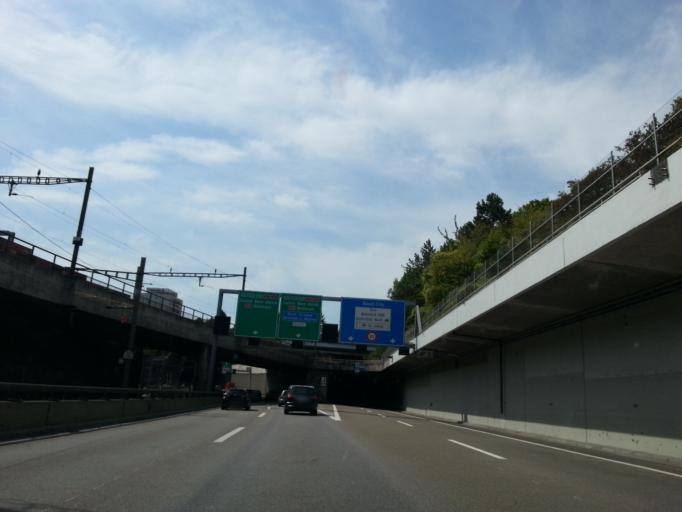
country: CH
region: Basel-Landschaft
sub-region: Bezirk Arlesheim
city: Birsfelden
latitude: 47.5486
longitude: 7.6147
